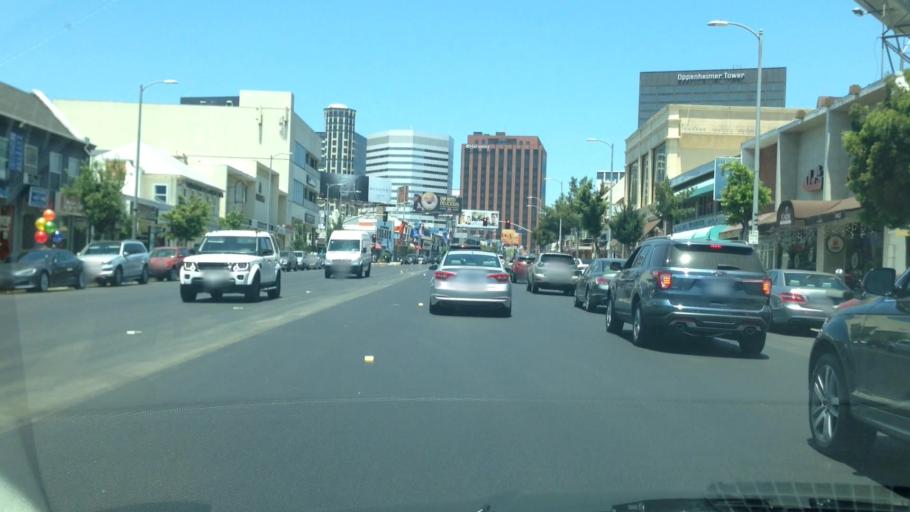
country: US
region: California
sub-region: Los Angeles County
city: Westwood, Los Angeles
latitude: 34.0543
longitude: -118.4409
